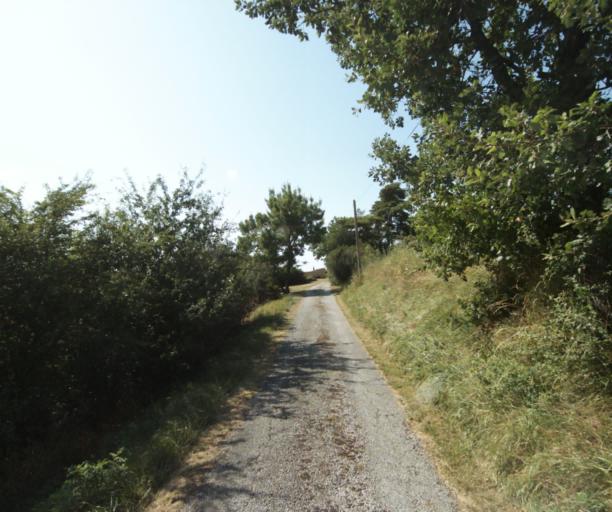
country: FR
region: Midi-Pyrenees
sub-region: Departement de la Haute-Garonne
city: Saint-Felix-Lauragais
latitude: 43.4315
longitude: 1.8436
